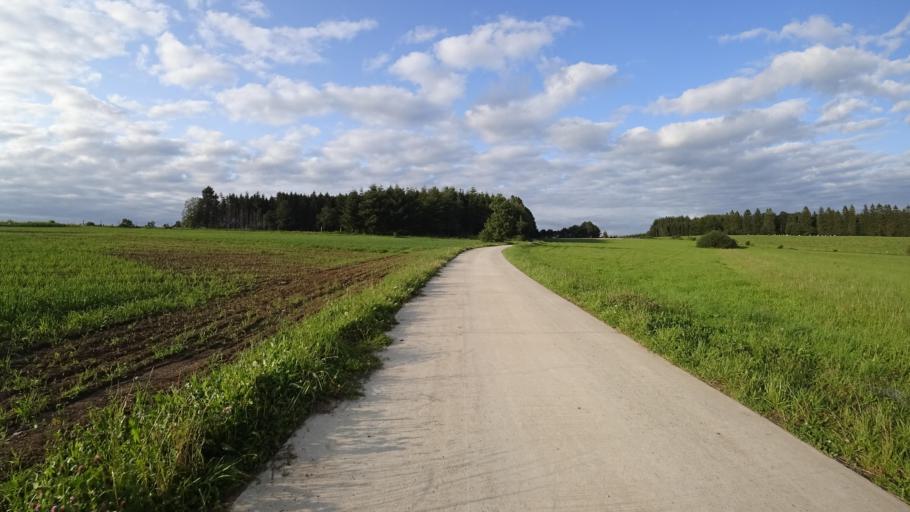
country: BE
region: Wallonia
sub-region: Province du Luxembourg
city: Neufchateau
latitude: 49.8448
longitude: 5.3462
